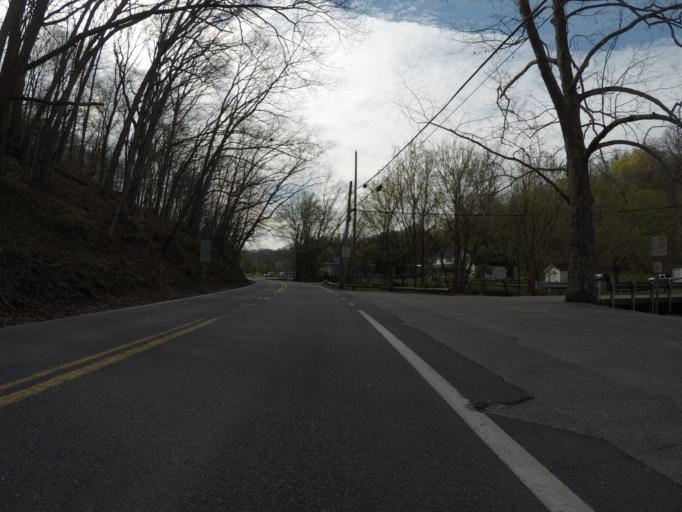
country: US
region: West Virginia
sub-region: Cabell County
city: Pea Ridge
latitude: 38.3823
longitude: -82.3764
